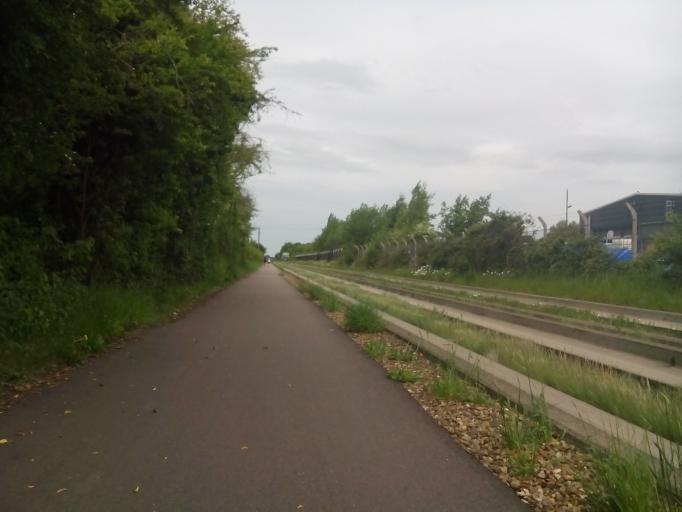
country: GB
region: England
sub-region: Cambridgeshire
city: Histon
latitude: 52.2472
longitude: 0.1019
